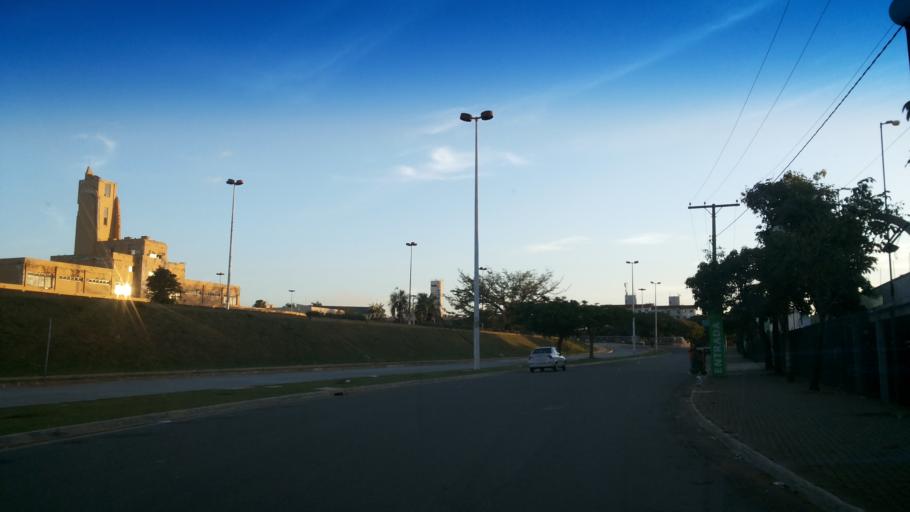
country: BR
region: Goias
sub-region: Goiania
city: Goiania
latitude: -16.6624
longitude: -49.2611
